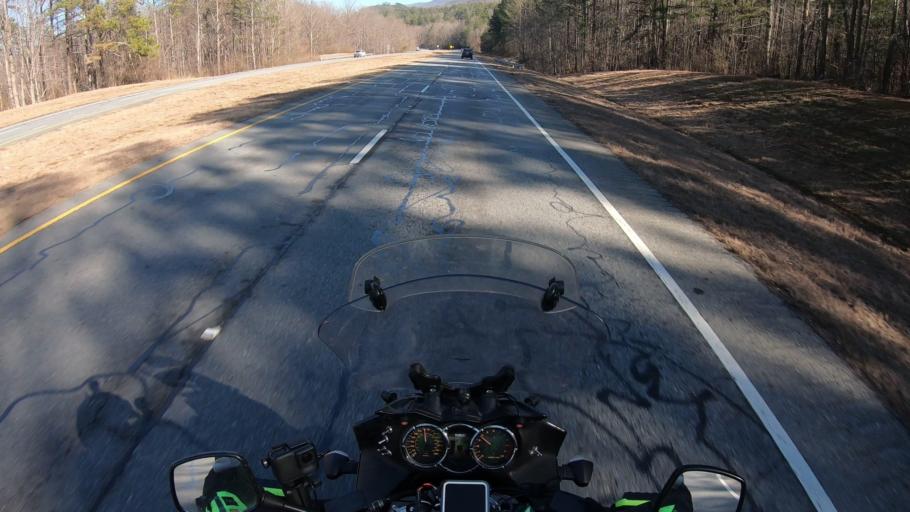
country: US
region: Georgia
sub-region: Gilmer County
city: Ellijay
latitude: 34.7246
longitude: -84.4419
